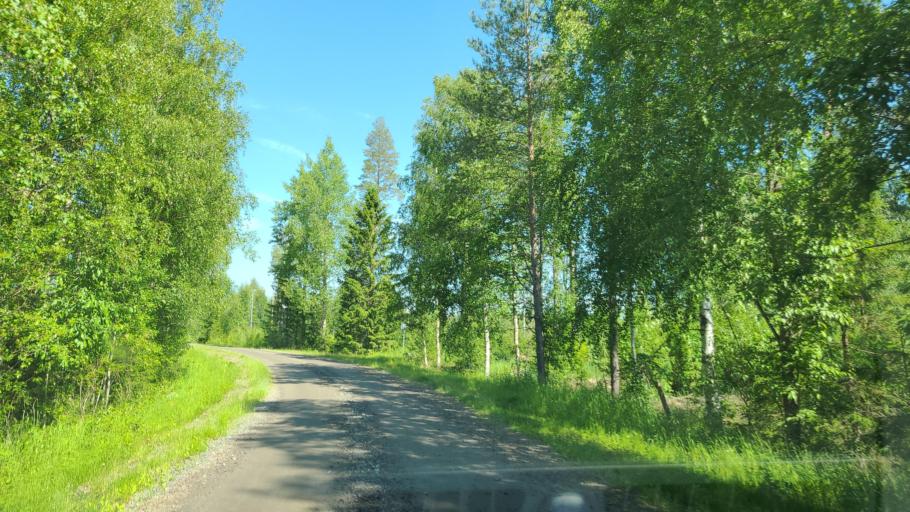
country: SE
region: Vaesterbotten
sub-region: Robertsfors Kommun
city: Robertsfors
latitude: 64.0891
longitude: 20.8494
